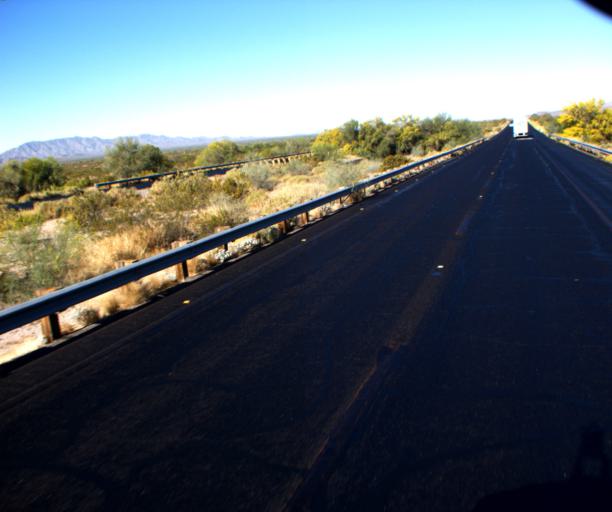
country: US
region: Arizona
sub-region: Pinal County
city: Maricopa
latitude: 32.8377
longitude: -112.2170
